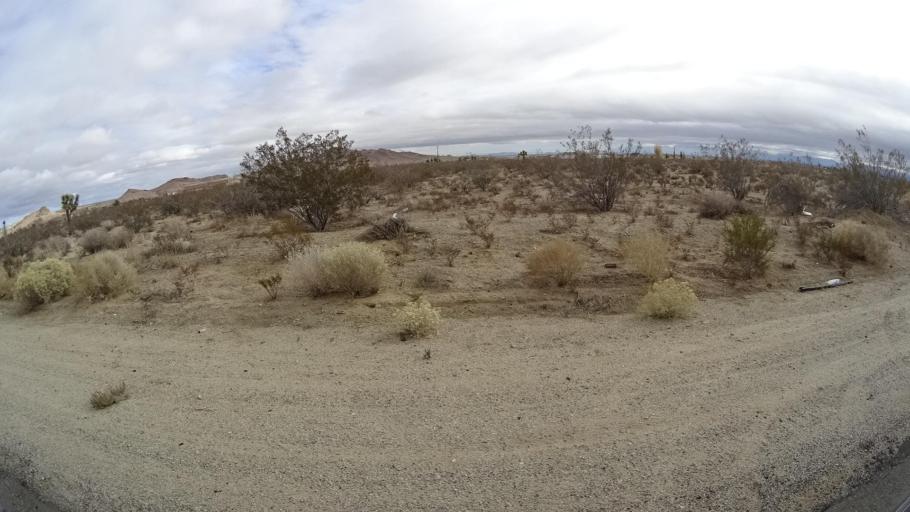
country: US
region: California
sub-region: Kern County
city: Rosamond
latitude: 34.8892
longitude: -118.2227
